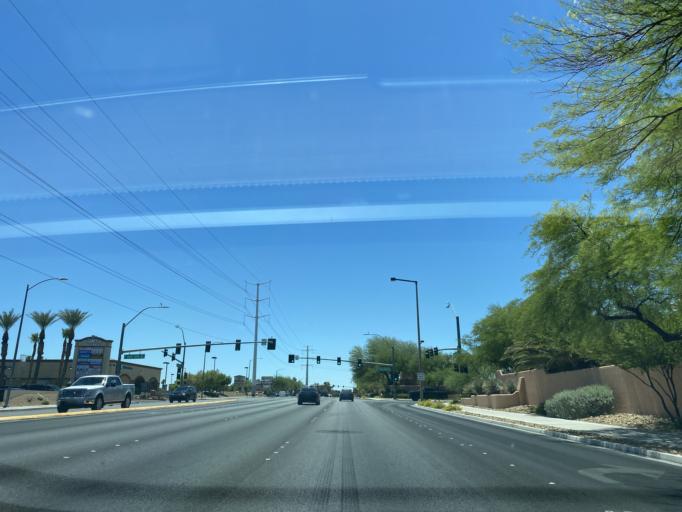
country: US
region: Nevada
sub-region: Clark County
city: Spring Valley
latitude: 36.1918
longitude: -115.2603
